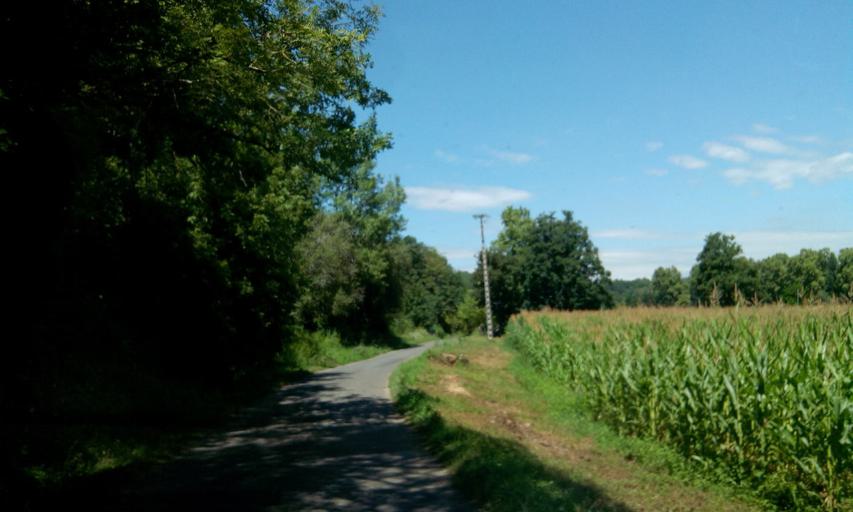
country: FR
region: Limousin
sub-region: Departement de la Correze
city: Meyssac
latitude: 45.0388
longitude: 1.6011
